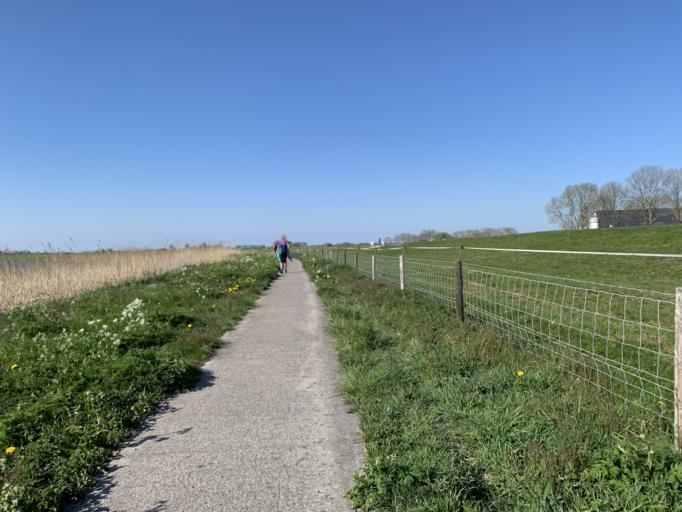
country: NL
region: Groningen
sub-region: Gemeente Winsum
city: Winsum
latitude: 53.2946
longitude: 6.5049
